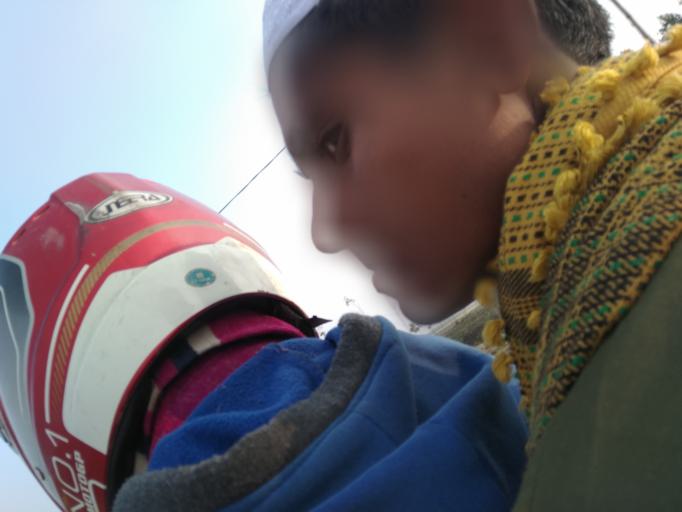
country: BD
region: Rajshahi
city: Ishurdi
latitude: 24.4864
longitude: 89.2123
